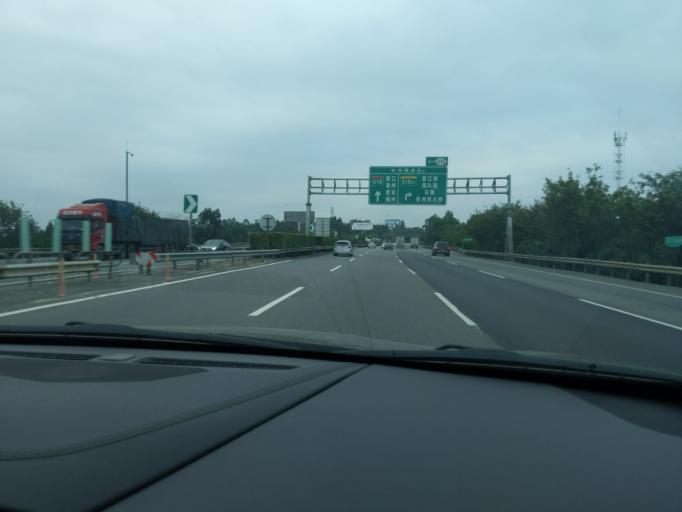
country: CN
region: Fujian
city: Neikeng
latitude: 24.7695
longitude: 118.4528
